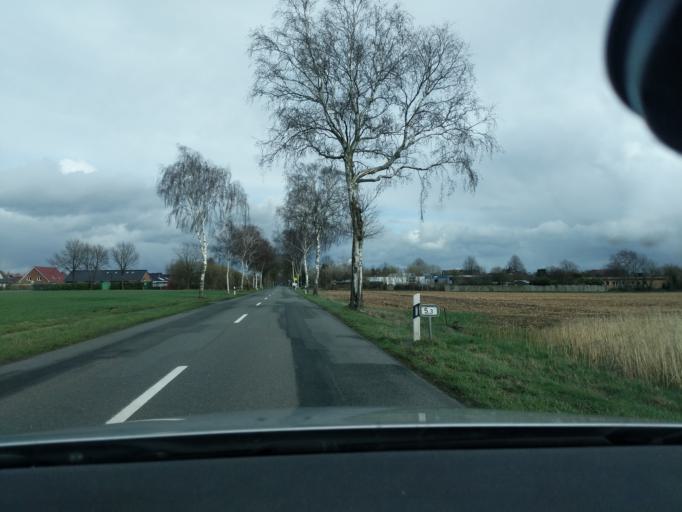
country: DE
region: Lower Saxony
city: Oldendorf
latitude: 53.5884
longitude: 9.2363
